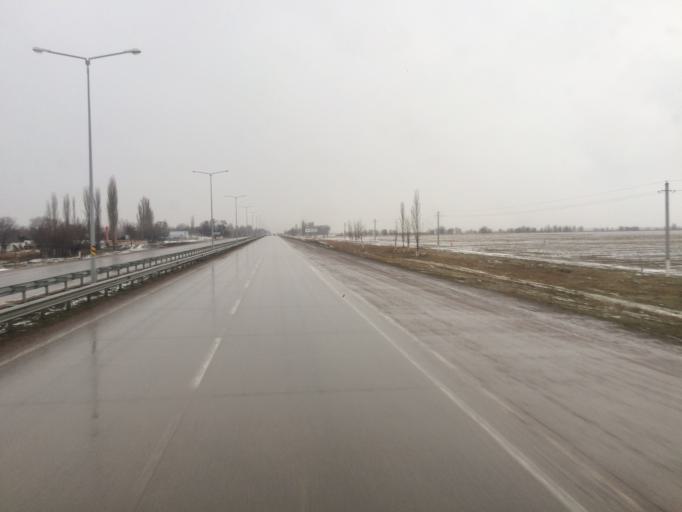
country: KZ
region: Zhambyl
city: Merke
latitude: 42.8765
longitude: 73.1134
